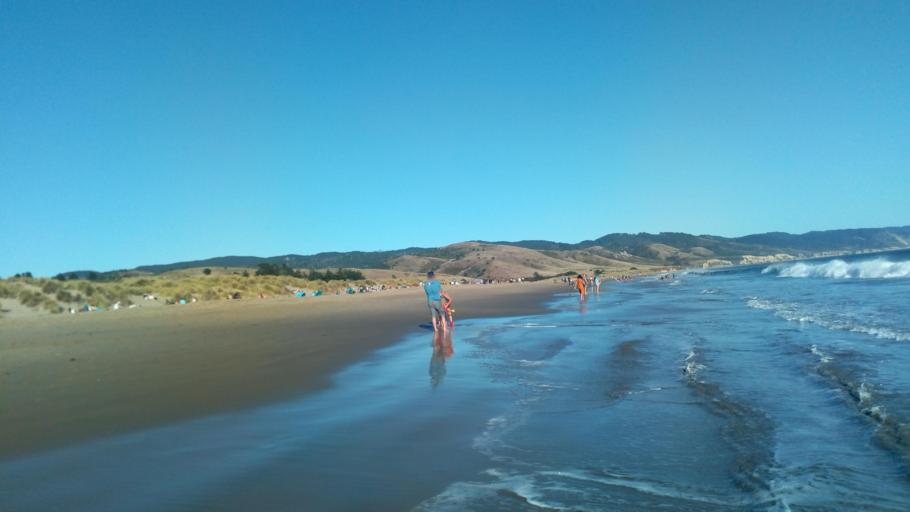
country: US
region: California
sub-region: Marin County
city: Inverness
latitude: 38.0255
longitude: -122.8853
